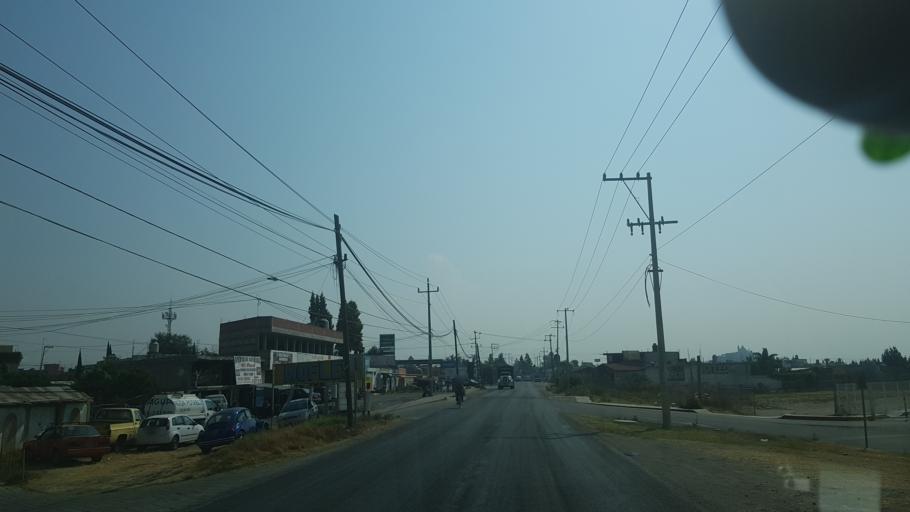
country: MX
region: Puebla
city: Cholula
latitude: 19.0576
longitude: -98.3215
